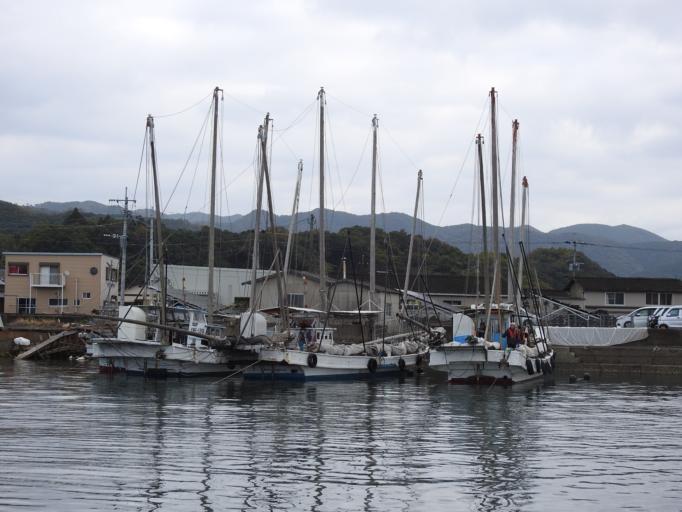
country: JP
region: Kumamoto
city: Minamata
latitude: 32.3002
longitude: 130.4830
